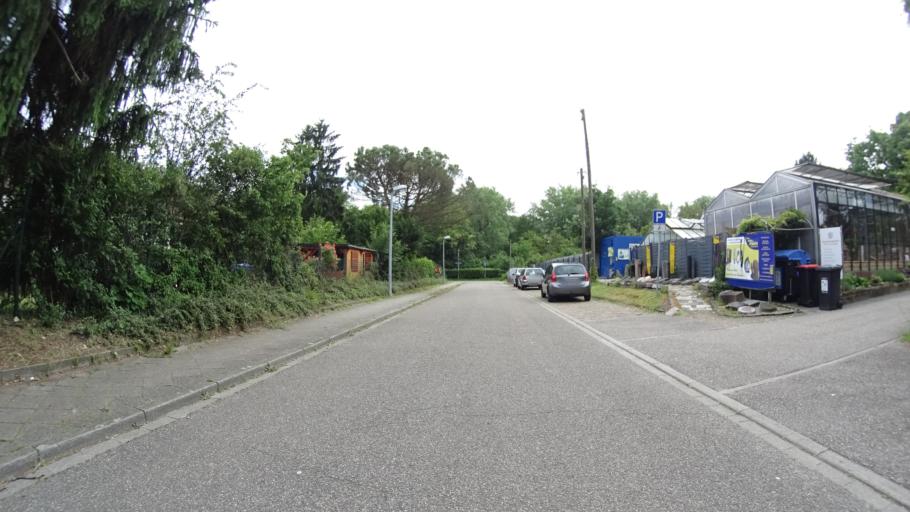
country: DE
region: Baden-Wuerttemberg
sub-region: Karlsruhe Region
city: Rheinstetten
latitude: 49.0068
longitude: 8.3393
